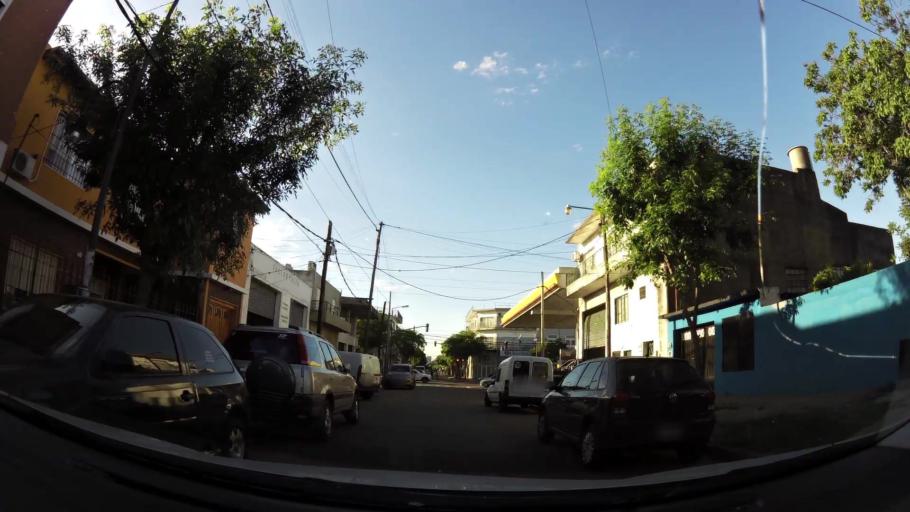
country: AR
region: Buenos Aires
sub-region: Partido de Tigre
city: Tigre
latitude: -34.4586
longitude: -58.5669
